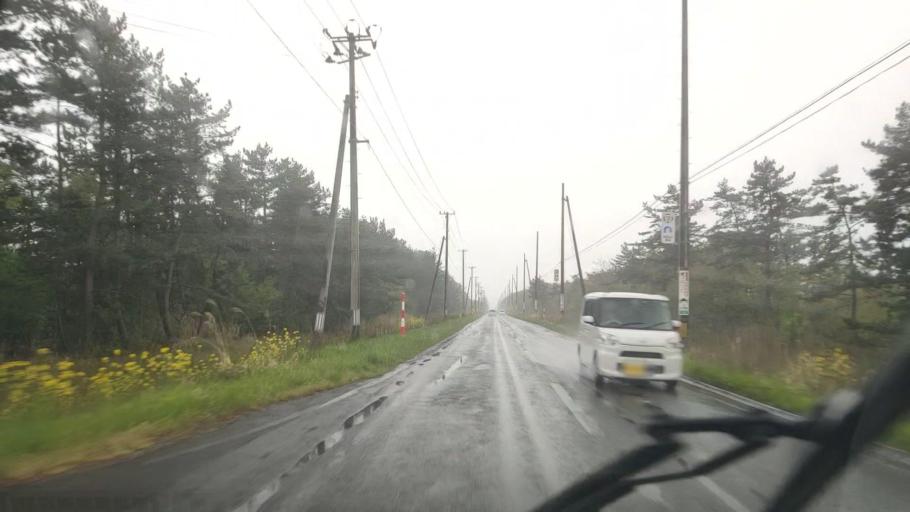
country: JP
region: Akita
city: Tenno
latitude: 40.0097
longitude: 139.9515
